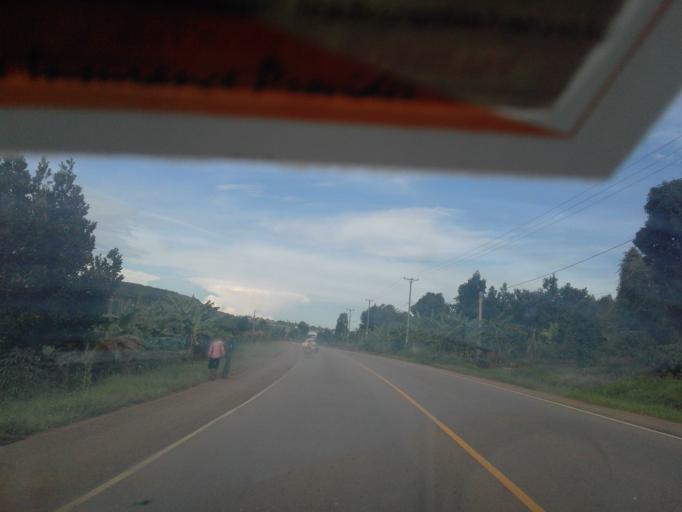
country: UG
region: Central Region
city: Masaka
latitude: -0.3422
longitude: 31.6349
